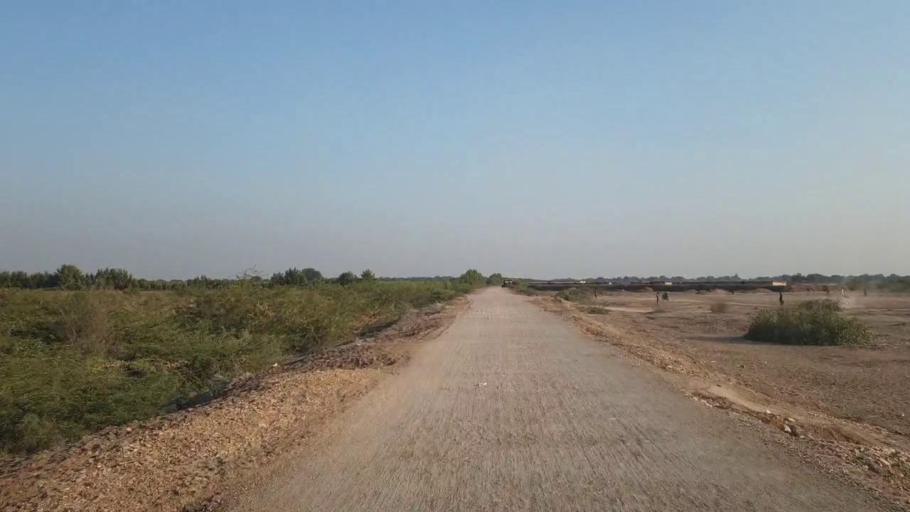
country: PK
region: Sindh
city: Mirpur Khas
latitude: 25.4253
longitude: 68.9030
